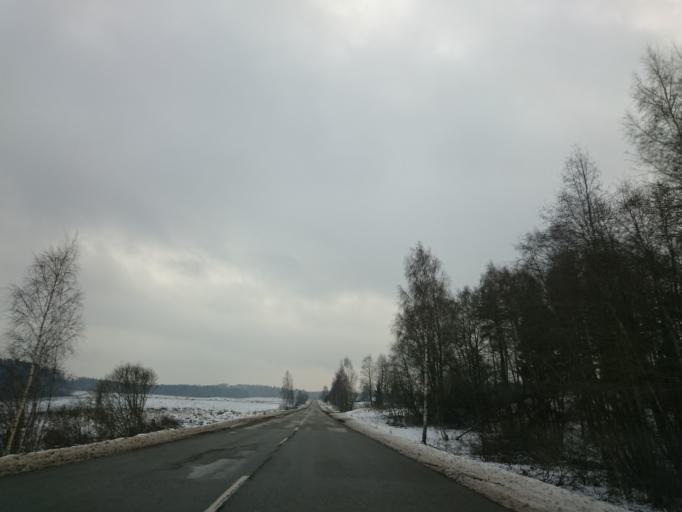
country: LV
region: Pargaujas
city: Stalbe
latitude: 57.3696
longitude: 25.0515
